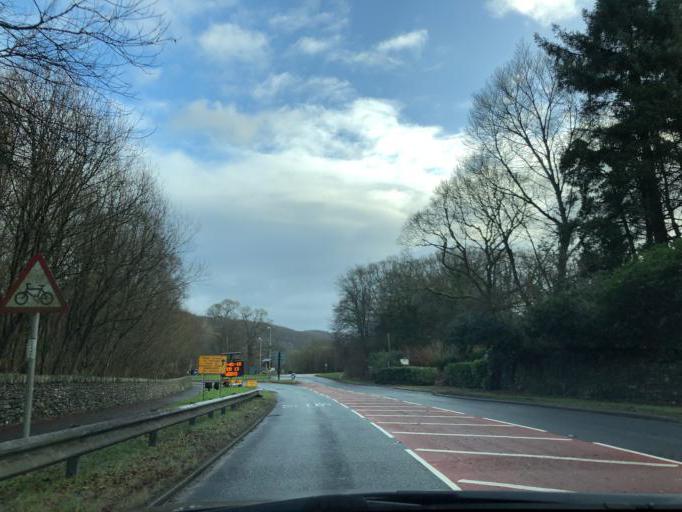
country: GB
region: England
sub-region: Cumbria
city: Grange-over-Sands
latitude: 54.2675
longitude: -2.9689
